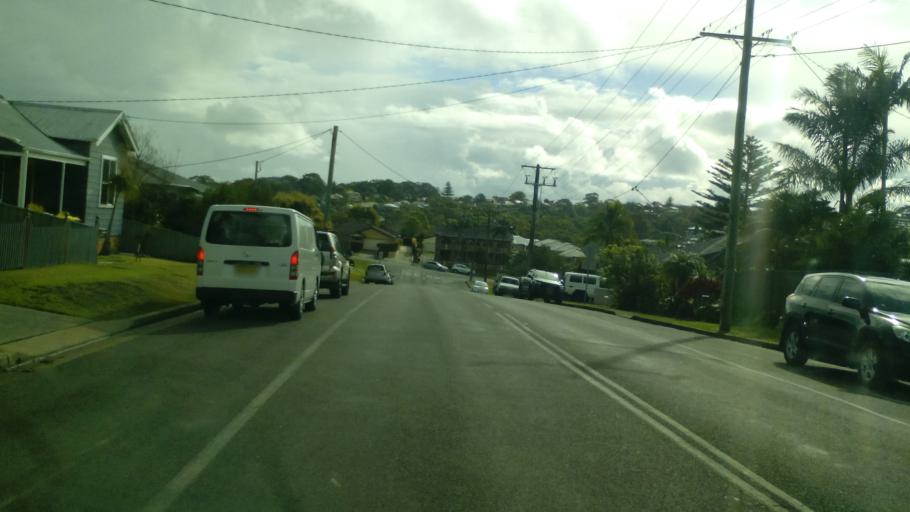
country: AU
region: New South Wales
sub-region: Lake Macquarie Shire
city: Kahibah
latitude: -32.9618
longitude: 151.7121
